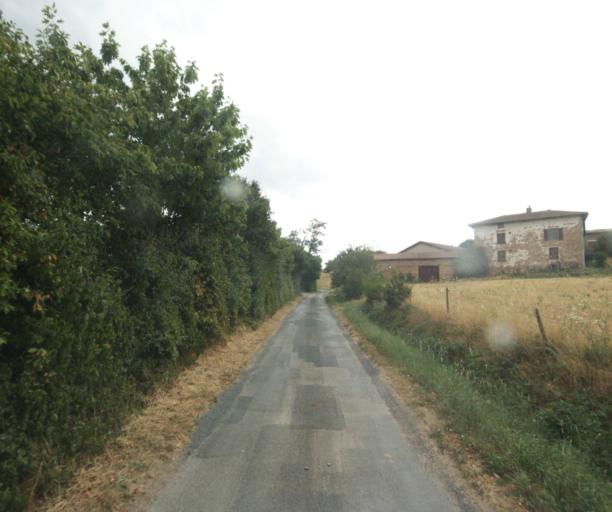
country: FR
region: Rhone-Alpes
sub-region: Departement du Rhone
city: Saint-Verand
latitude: 45.8867
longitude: 4.5540
